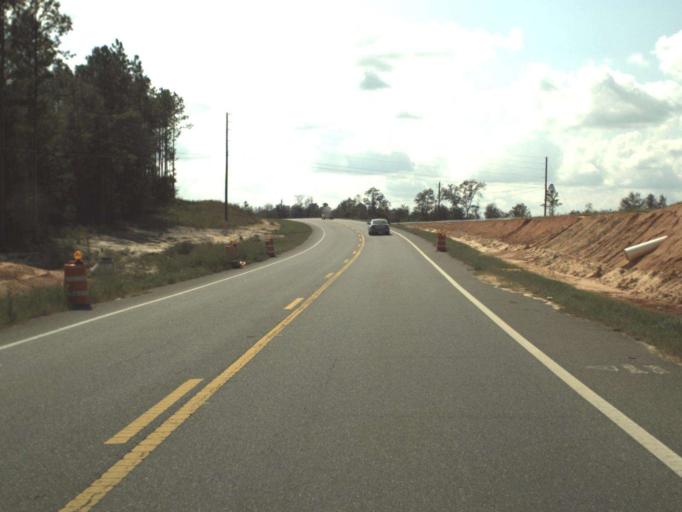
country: US
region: Florida
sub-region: Holmes County
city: Bonifay
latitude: 30.6648
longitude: -85.6940
